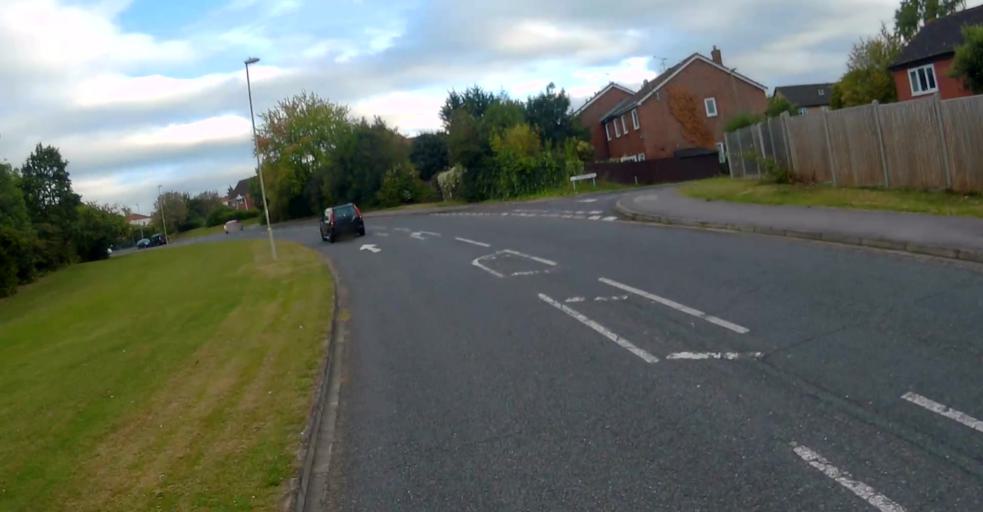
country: GB
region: England
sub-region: Hampshire
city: Basingstoke
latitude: 51.2415
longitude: -1.1244
